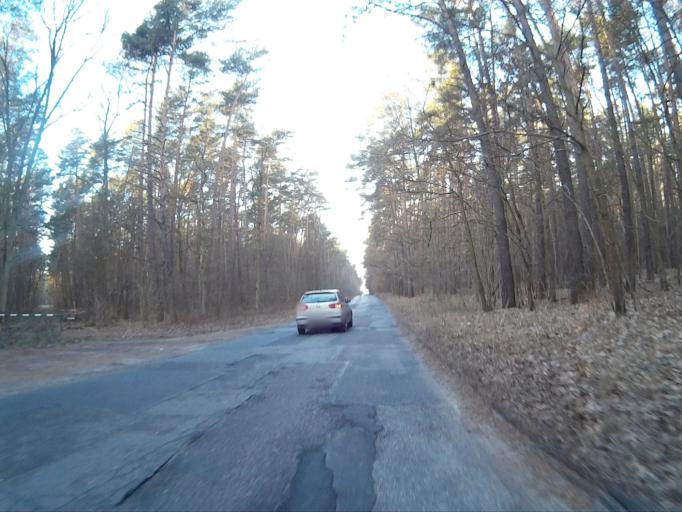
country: PL
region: Kujawsko-Pomorskie
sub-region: Powiat bydgoski
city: Osielsko
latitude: 53.1604
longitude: 18.0672
